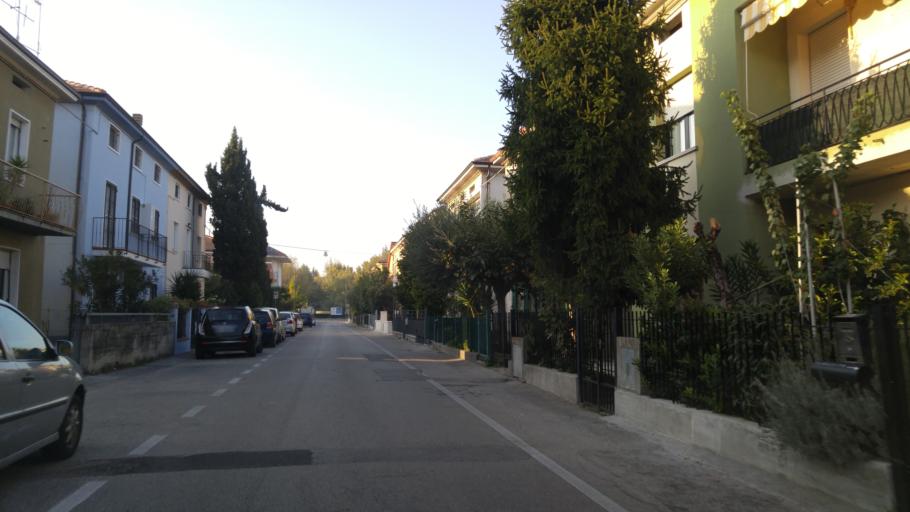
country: IT
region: The Marches
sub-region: Provincia di Pesaro e Urbino
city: Pesaro
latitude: 43.8962
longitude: 12.8890
